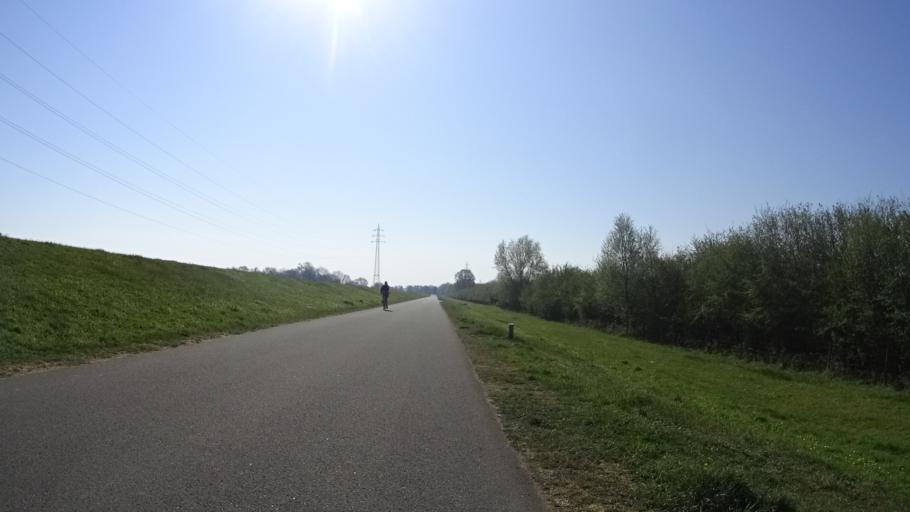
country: DE
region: North Rhine-Westphalia
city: Rheinberg
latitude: 51.5758
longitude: 6.5834
